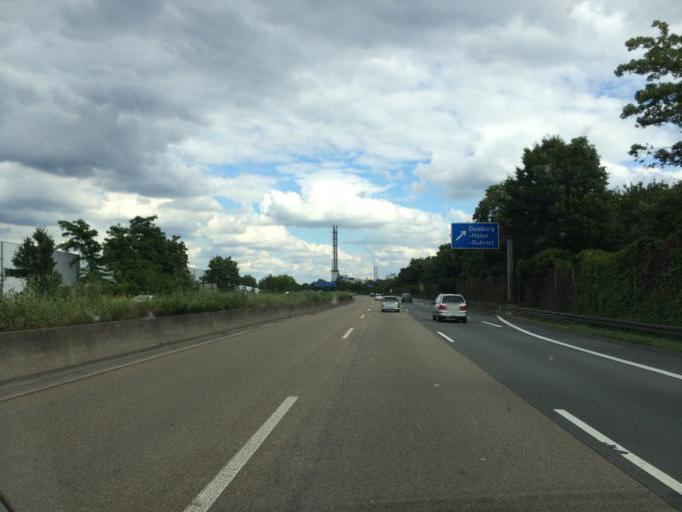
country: DE
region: North Rhine-Westphalia
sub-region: Regierungsbezirk Dusseldorf
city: Hochfeld
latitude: 51.4373
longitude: 6.7319
